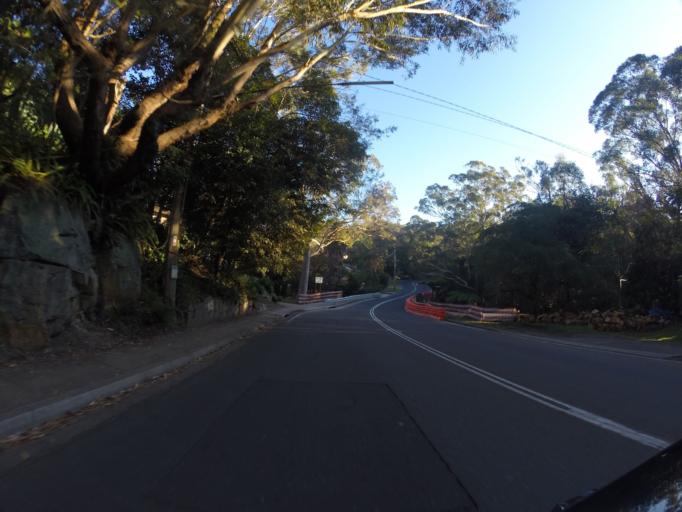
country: AU
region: New South Wales
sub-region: Sutherland Shire
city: Gymea Bay
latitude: -34.0497
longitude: 151.0762
